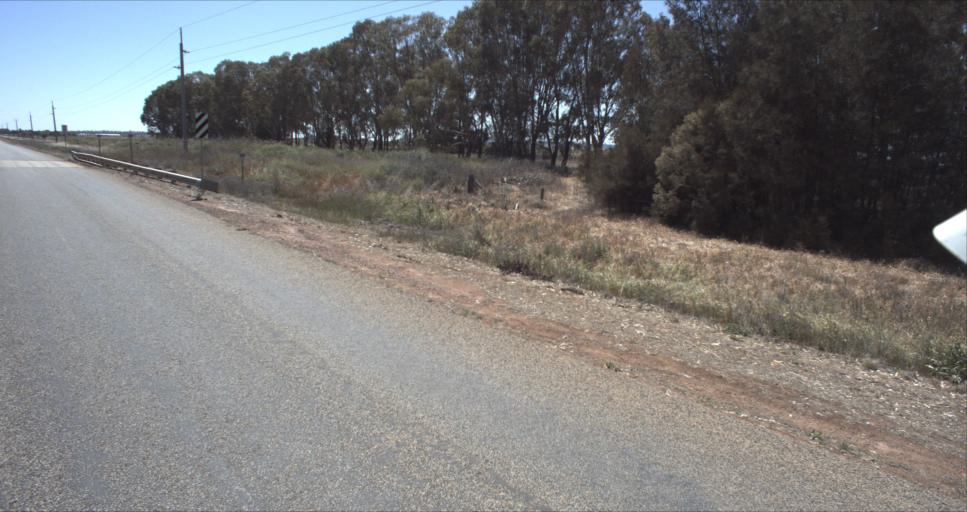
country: AU
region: New South Wales
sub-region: Leeton
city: Leeton
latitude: -34.4652
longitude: 146.2934
